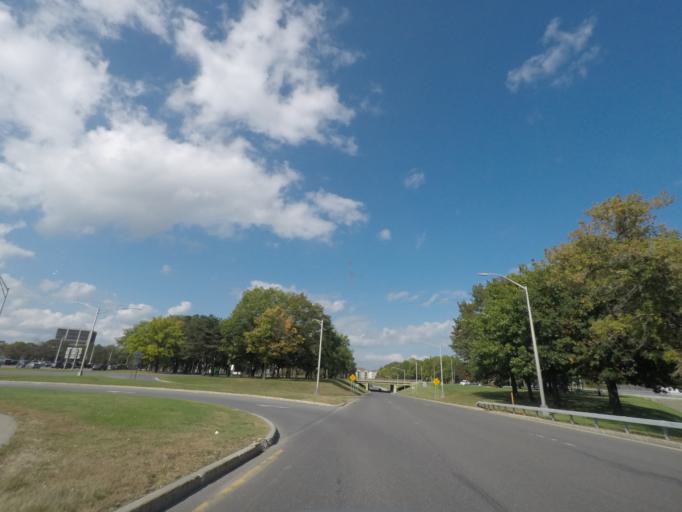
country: US
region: New York
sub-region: Albany County
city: Roessleville
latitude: 42.6781
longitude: -73.8026
